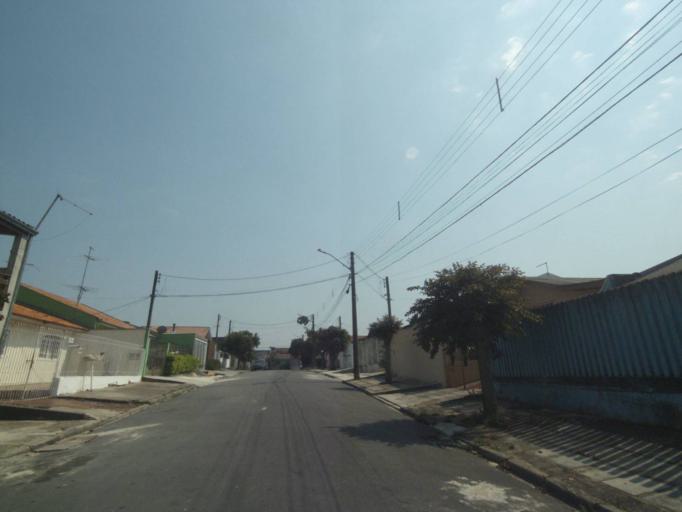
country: BR
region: Parana
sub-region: Sao Jose Dos Pinhais
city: Sao Jose dos Pinhais
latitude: -25.5322
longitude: -49.2491
